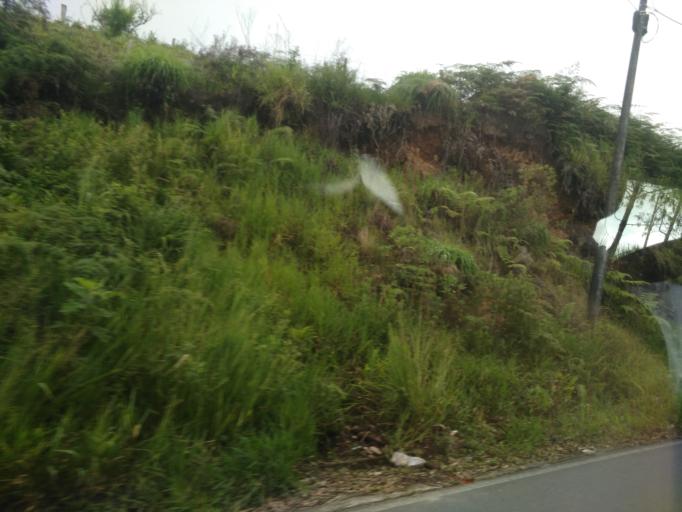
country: CO
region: Valle del Cauca
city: Sevilla
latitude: 4.2716
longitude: -75.9158
